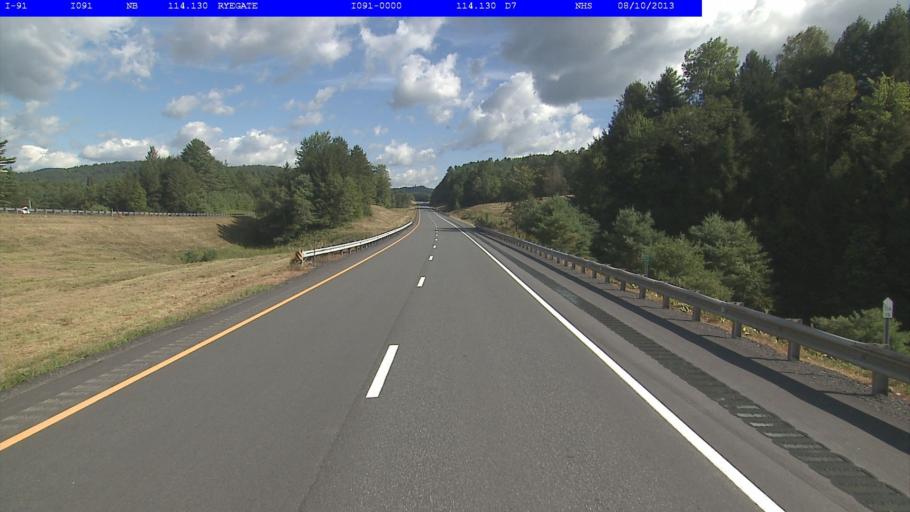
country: US
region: New Hampshire
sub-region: Grafton County
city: Woodsville
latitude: 44.2122
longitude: -72.0671
